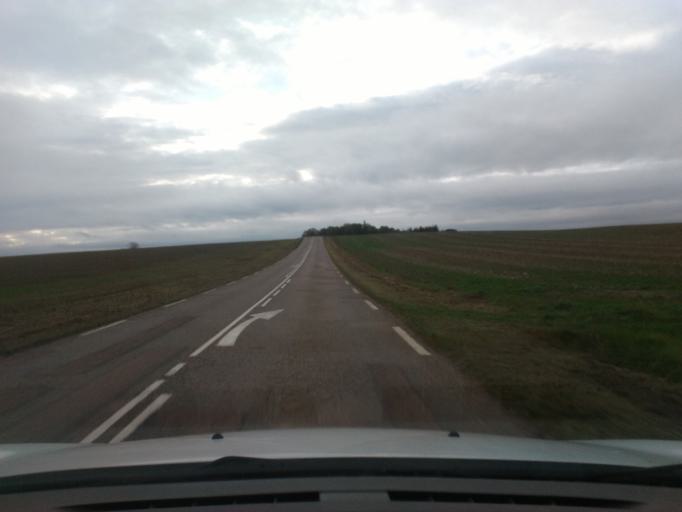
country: FR
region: Lorraine
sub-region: Departement des Vosges
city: Rambervillers
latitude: 48.3555
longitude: 6.5961
